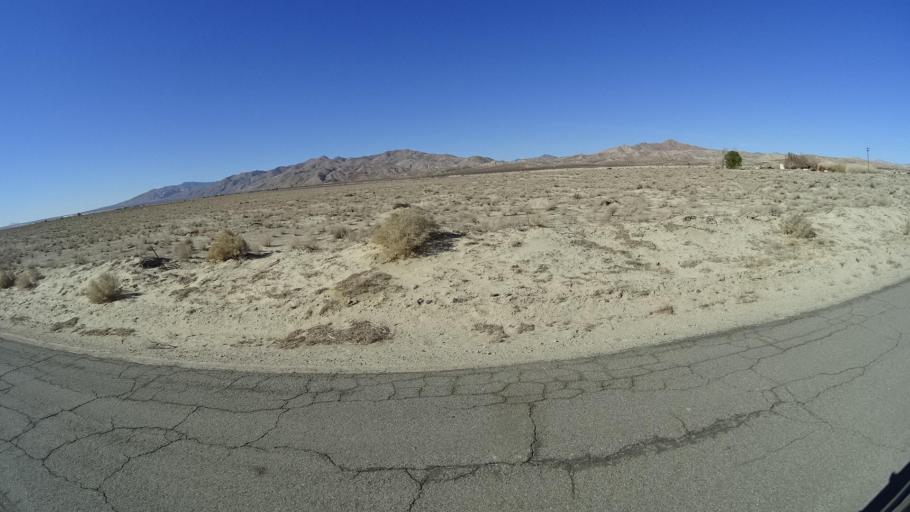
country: US
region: California
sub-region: Kern County
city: California City
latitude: 35.3041
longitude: -117.9680
